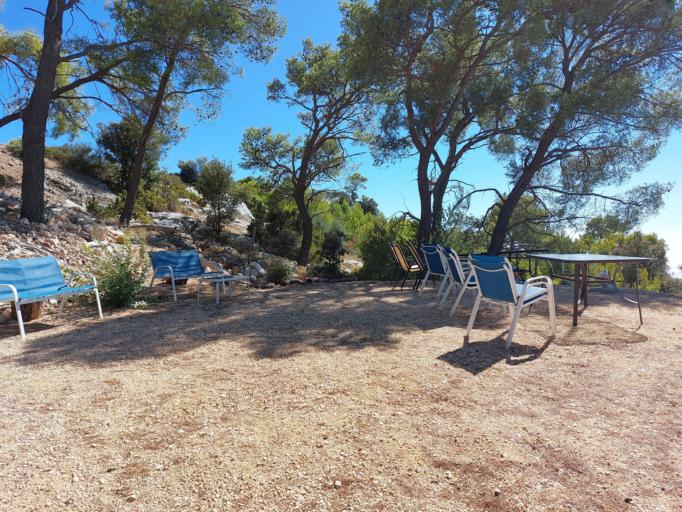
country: HR
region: Dubrovacko-Neretvanska
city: Smokvica
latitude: 42.7410
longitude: 16.8402
